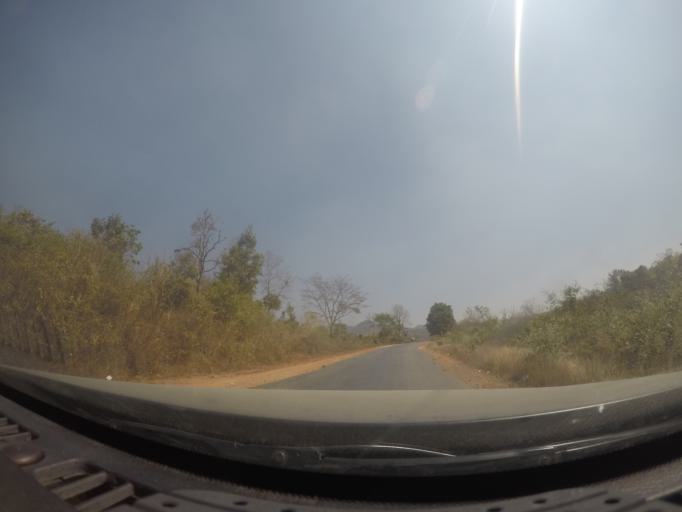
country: MM
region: Shan
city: Taunggyi
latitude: 20.8117
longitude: 97.2391
